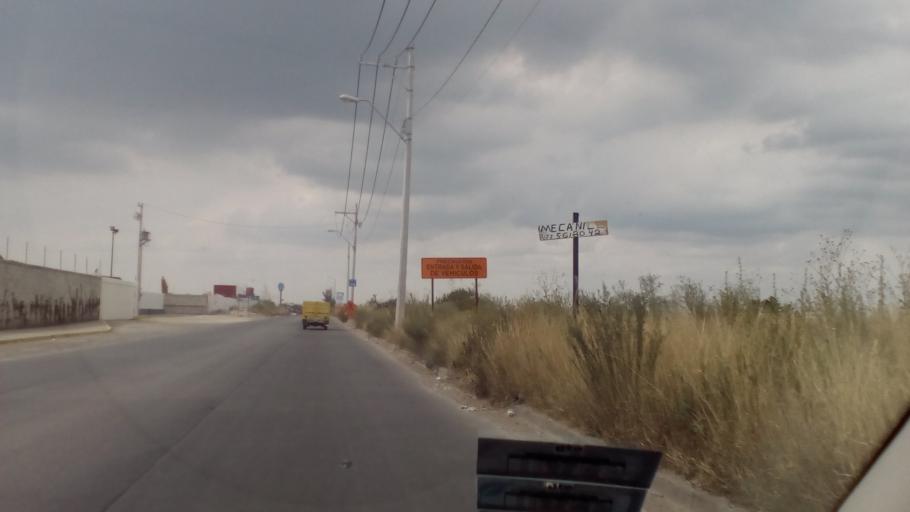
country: MX
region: Guanajuato
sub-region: Leon
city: Fraccionamiento Paseo de las Torres
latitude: 21.1716
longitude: -101.7535
